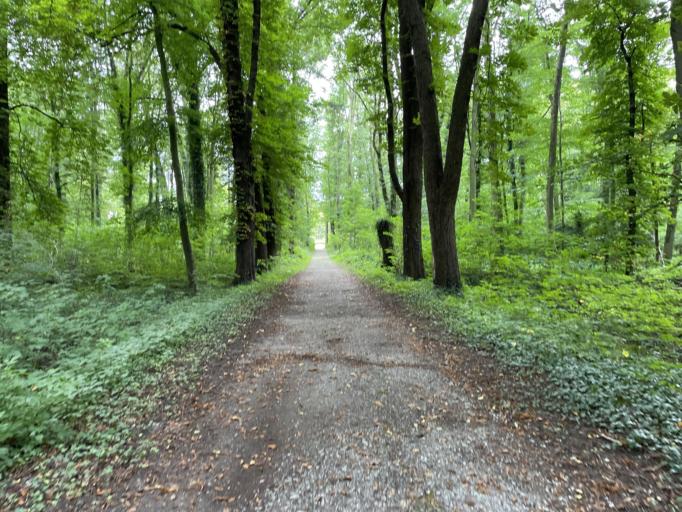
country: DE
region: North Rhine-Westphalia
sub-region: Regierungsbezirk Munster
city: Altenberge
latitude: 51.9739
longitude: 7.5053
